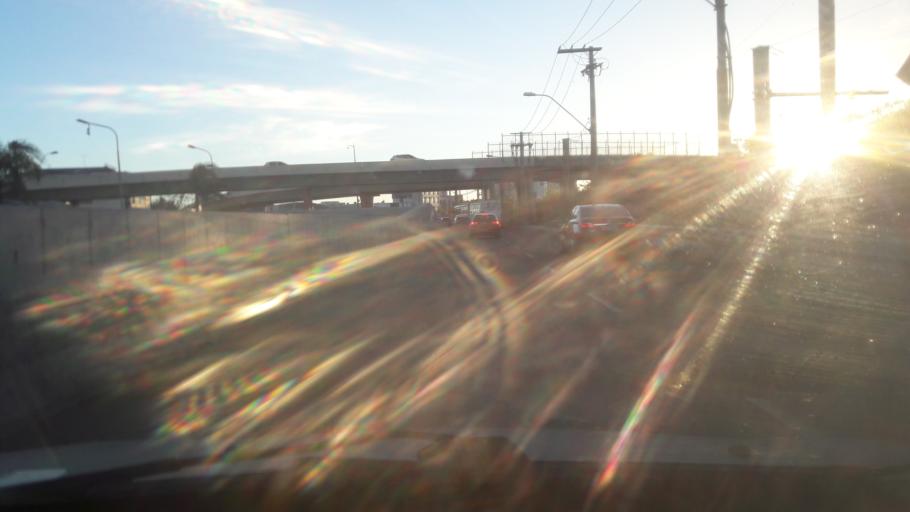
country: BR
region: Rio Grande do Sul
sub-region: Porto Alegre
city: Porto Alegre
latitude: -29.9952
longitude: -51.1889
